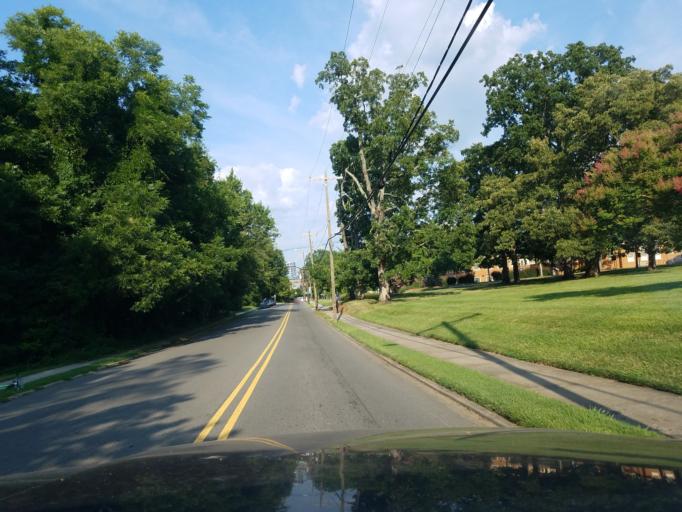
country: US
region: North Carolina
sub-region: Durham County
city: Durham
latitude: 35.9916
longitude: -78.9111
